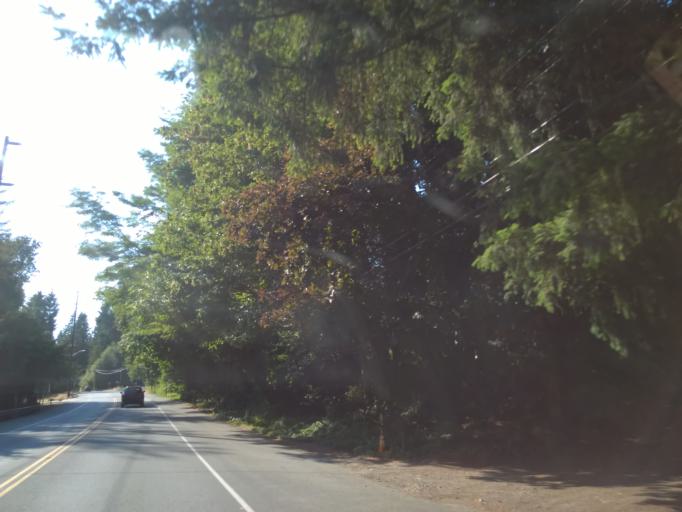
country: US
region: Washington
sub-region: King County
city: Cottage Lake
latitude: 47.7596
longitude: -122.0911
